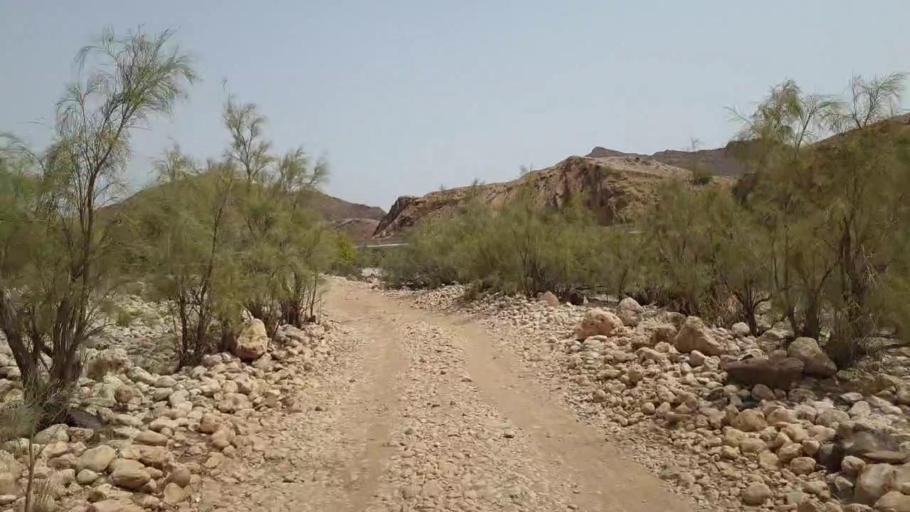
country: PK
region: Sindh
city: Sann
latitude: 25.8845
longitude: 67.9219
